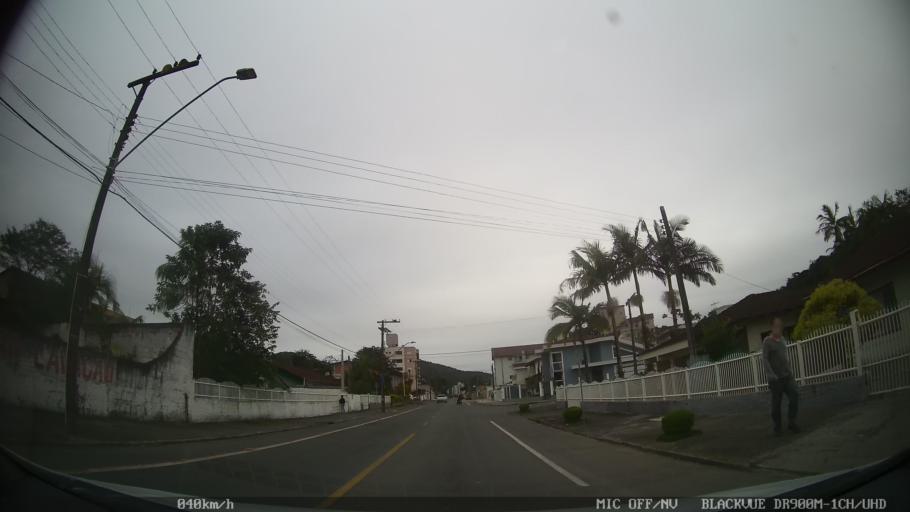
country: BR
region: Santa Catarina
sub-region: Joinville
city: Joinville
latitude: -26.2765
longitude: -48.8417
